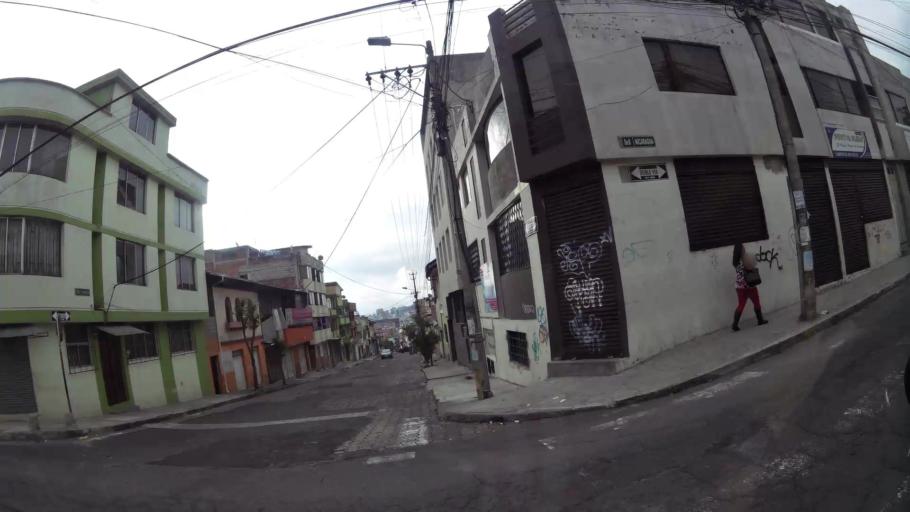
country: EC
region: Pichincha
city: Quito
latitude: -0.2067
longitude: -78.5090
